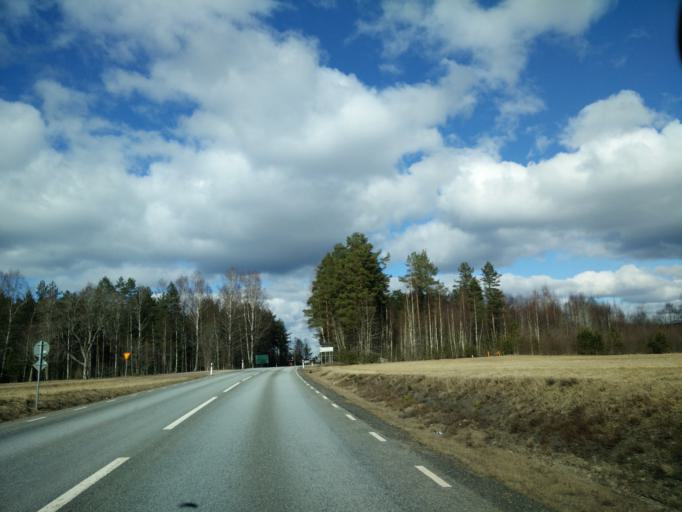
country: SE
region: Vaermland
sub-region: Hagfors Kommun
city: Hagfors
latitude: 59.9660
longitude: 13.5613
